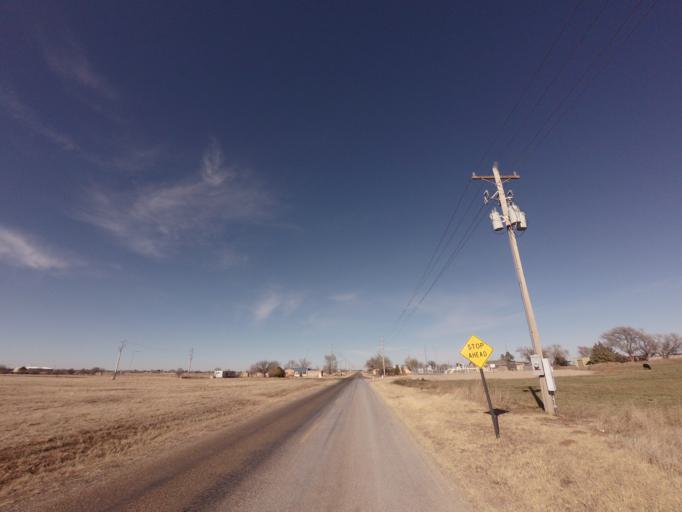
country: US
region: New Mexico
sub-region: Curry County
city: Clovis
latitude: 34.4040
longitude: -103.1611
